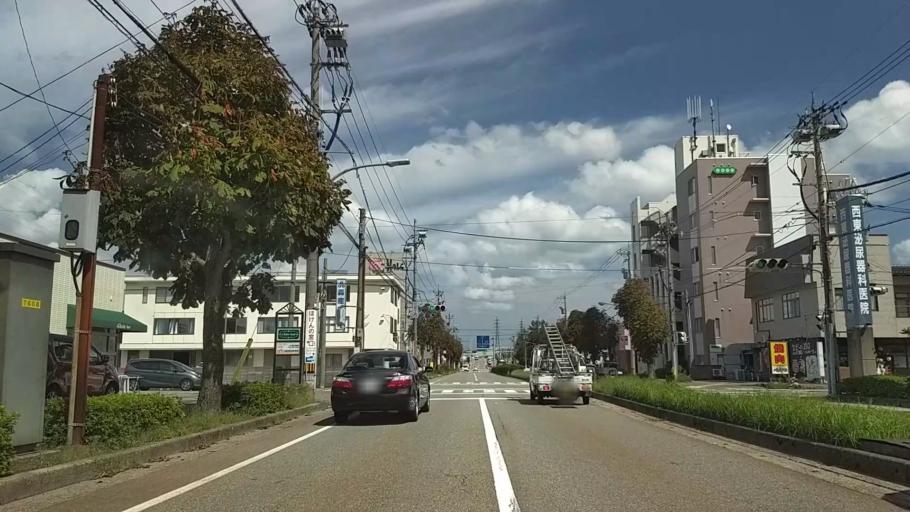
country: JP
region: Ishikawa
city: Kanazawa-shi
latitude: 36.5858
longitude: 136.6454
